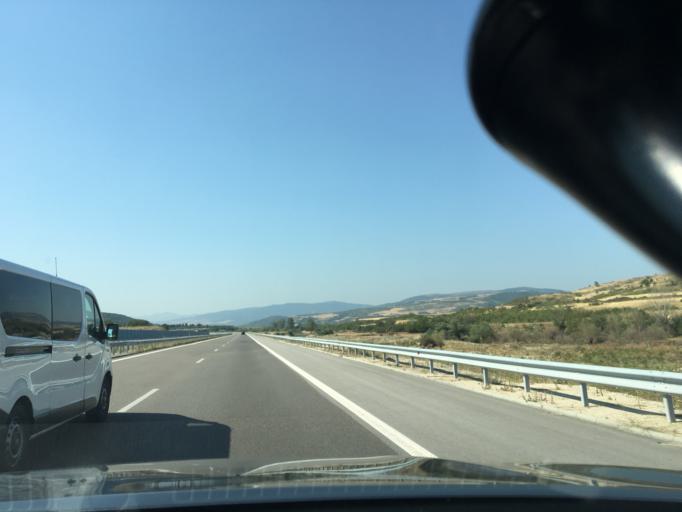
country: BG
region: Kyustendil
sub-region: Obshtina Dupnitsa
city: Dupnitsa
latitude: 42.2287
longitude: 23.0808
